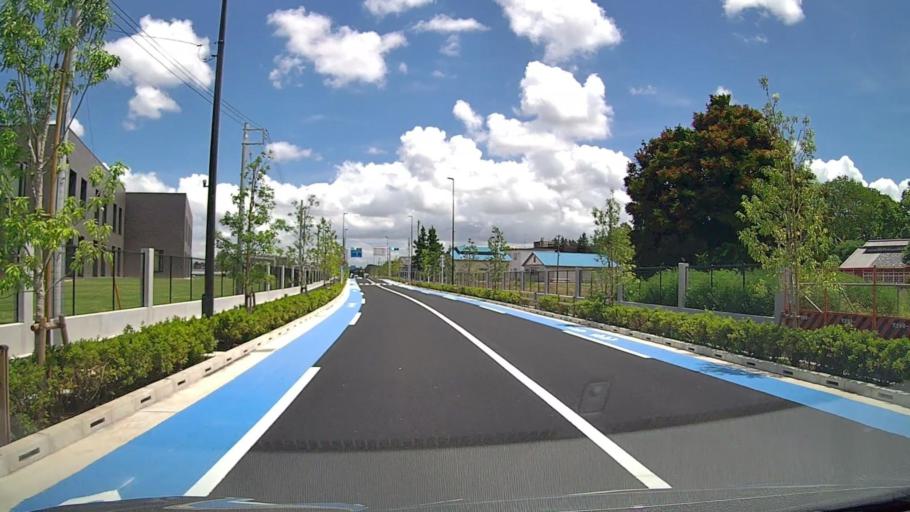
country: JP
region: Tokyo
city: Tanashicho
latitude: 35.7364
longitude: 139.5383
